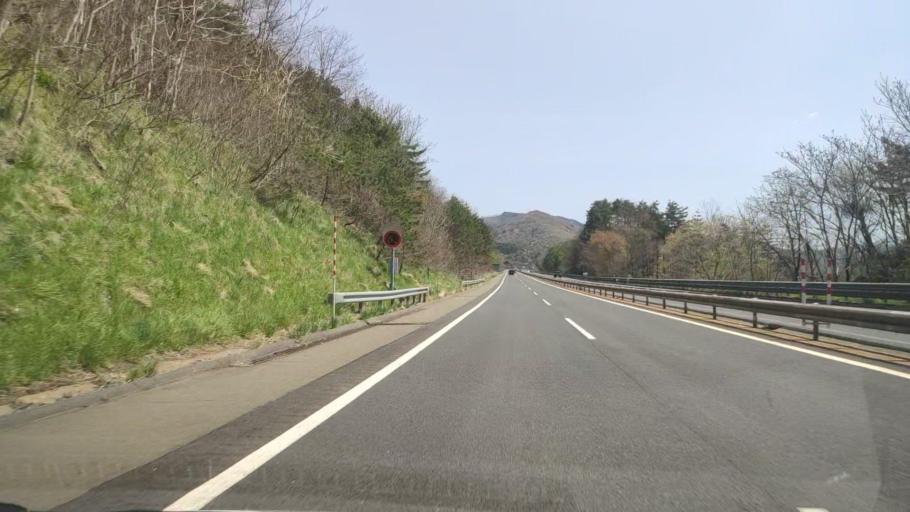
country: JP
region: Iwate
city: Ichinohe
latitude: 40.2296
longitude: 141.2852
